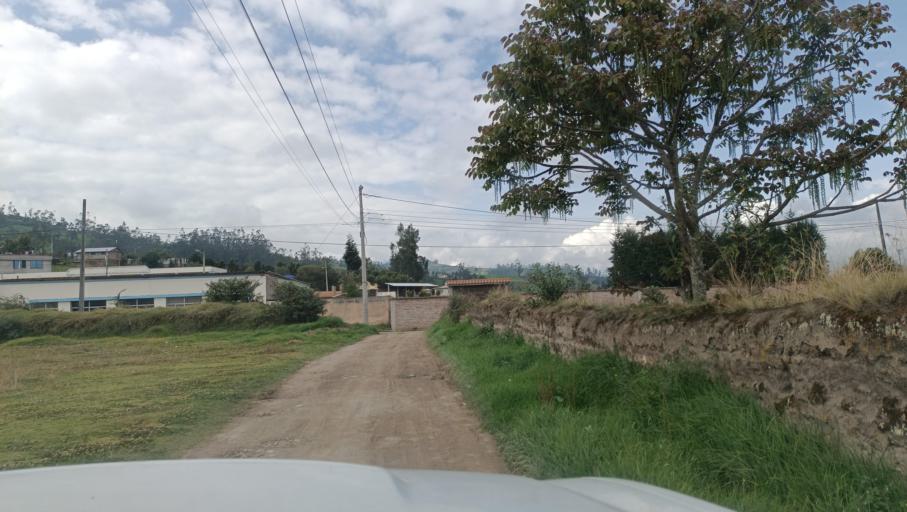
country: EC
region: Chimborazo
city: Guano
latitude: -1.6568
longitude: -78.5693
